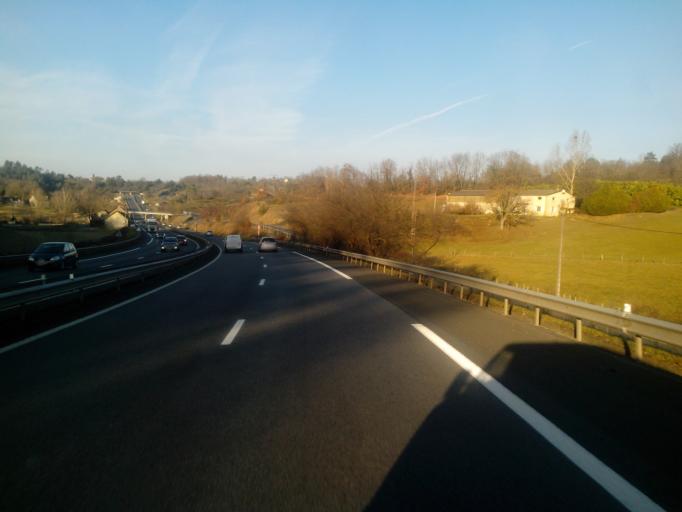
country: FR
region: Limousin
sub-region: Departement de la Correze
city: Brive-la-Gaillarde
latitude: 45.0872
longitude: 1.5190
